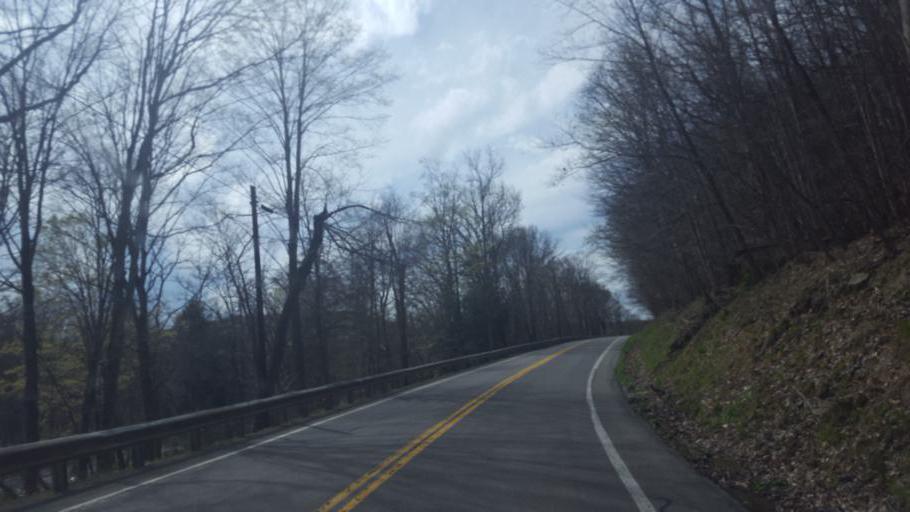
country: US
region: Pennsylvania
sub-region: Venango County
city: Sugarcreek
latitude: 41.3533
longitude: -79.9470
